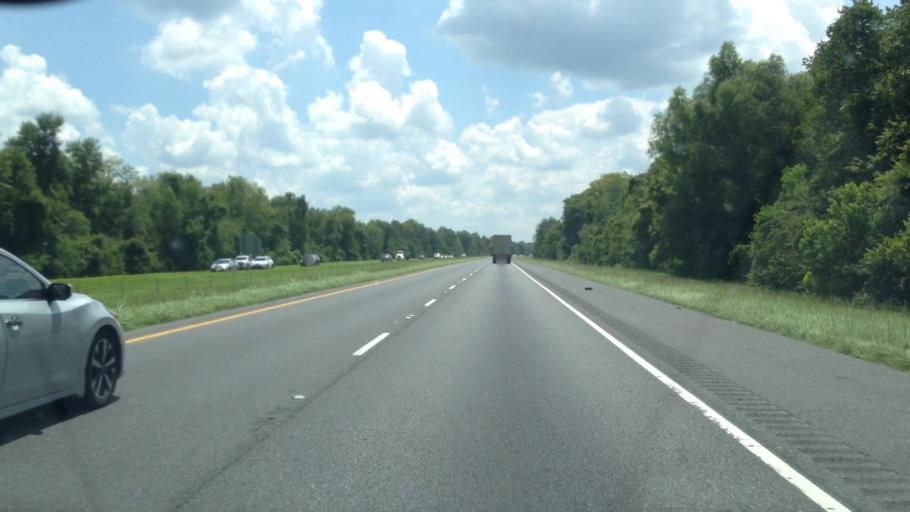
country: US
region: Louisiana
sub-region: Ascension Parish
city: Sorrento
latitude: 30.1501
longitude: -90.7852
